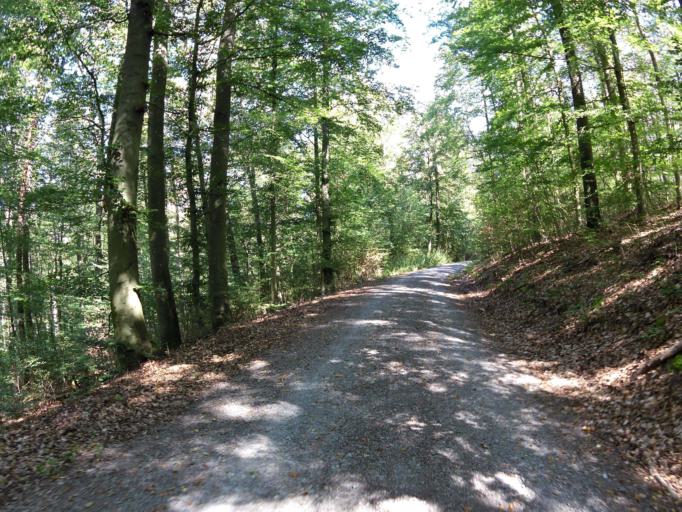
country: DE
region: Bavaria
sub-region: Regierungsbezirk Unterfranken
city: Thungersheim
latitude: 49.8673
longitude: 9.8702
